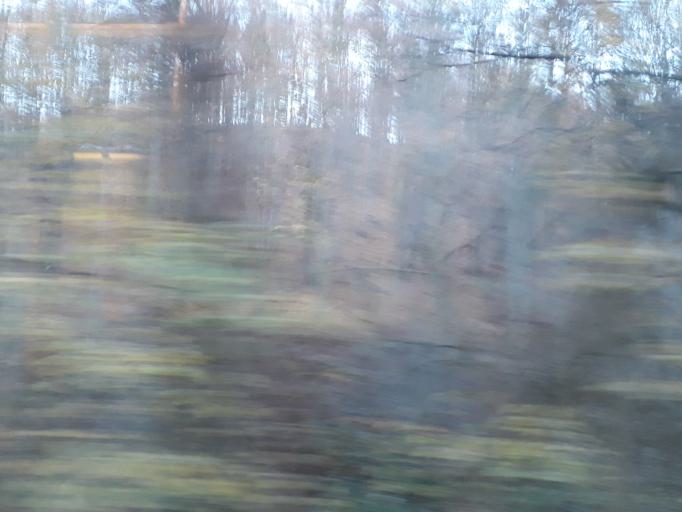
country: DE
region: Saxony
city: Reinhardtsgrimma
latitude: 50.9152
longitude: 13.7863
